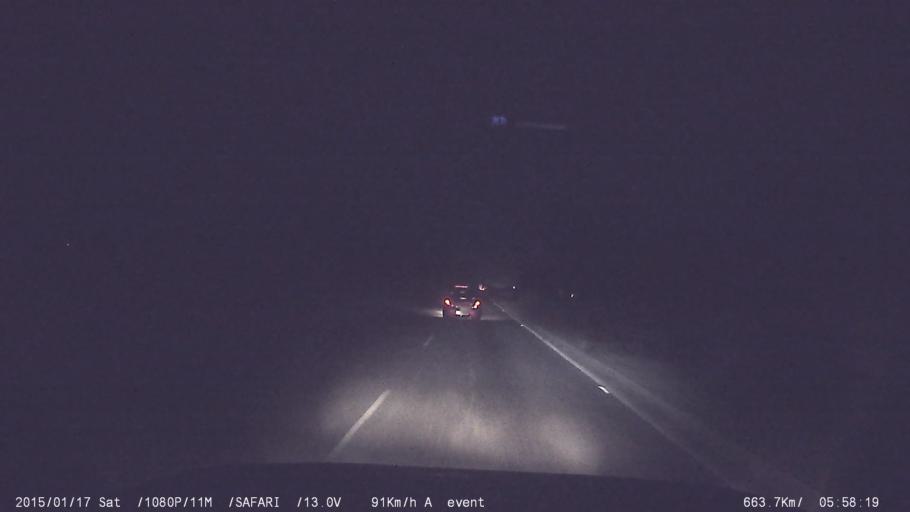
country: IN
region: Tamil Nadu
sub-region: Kancheepuram
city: Kanchipuram
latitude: 12.8984
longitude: 79.5516
